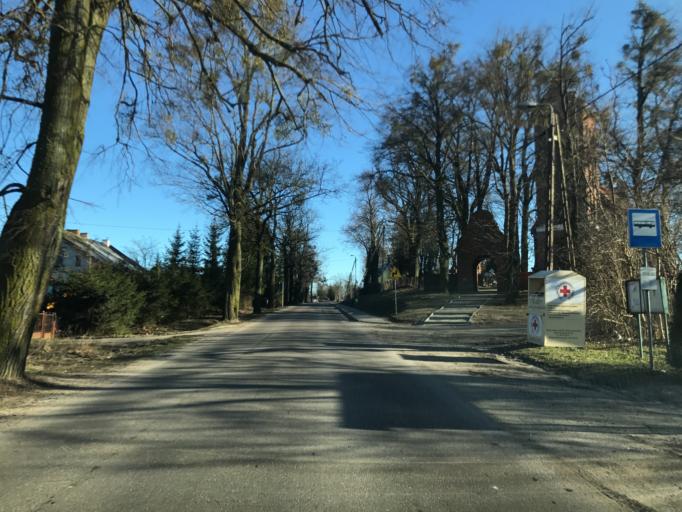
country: PL
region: Warmian-Masurian Voivodeship
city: Dobre Miasto
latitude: 53.9485
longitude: 20.3160
